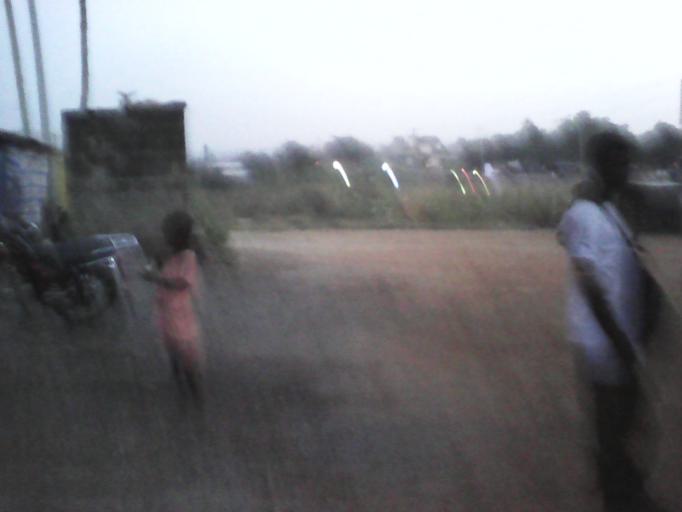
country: TG
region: Kara
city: Kara
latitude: 9.5558
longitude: 1.1950
